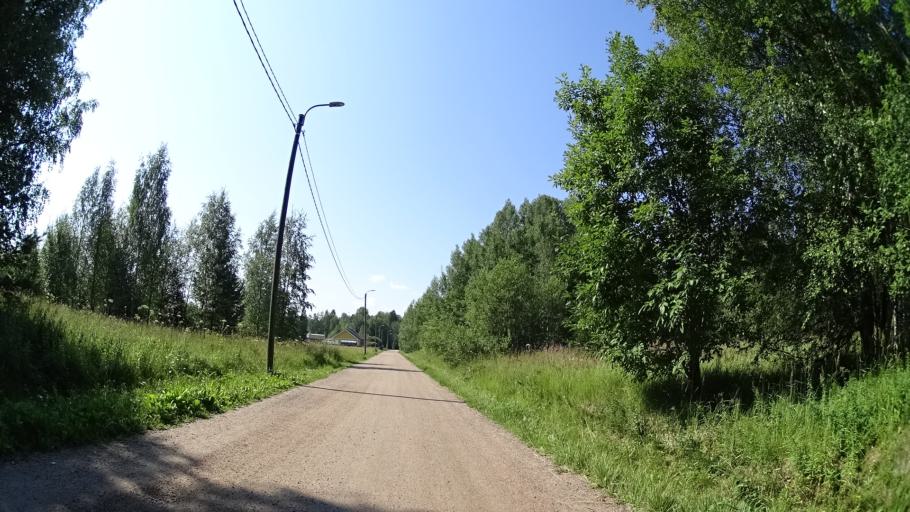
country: FI
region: Uusimaa
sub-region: Helsinki
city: Kerava
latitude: 60.3625
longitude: 25.0753
